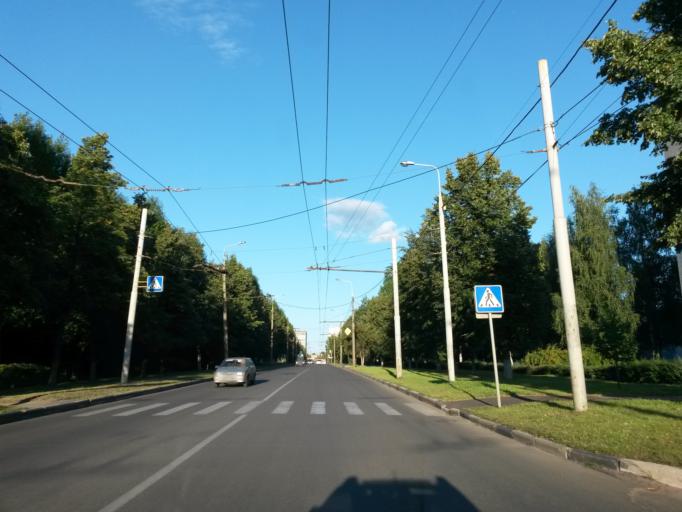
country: RU
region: Jaroslavl
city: Yaroslavl
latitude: 57.5906
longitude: 39.8511
